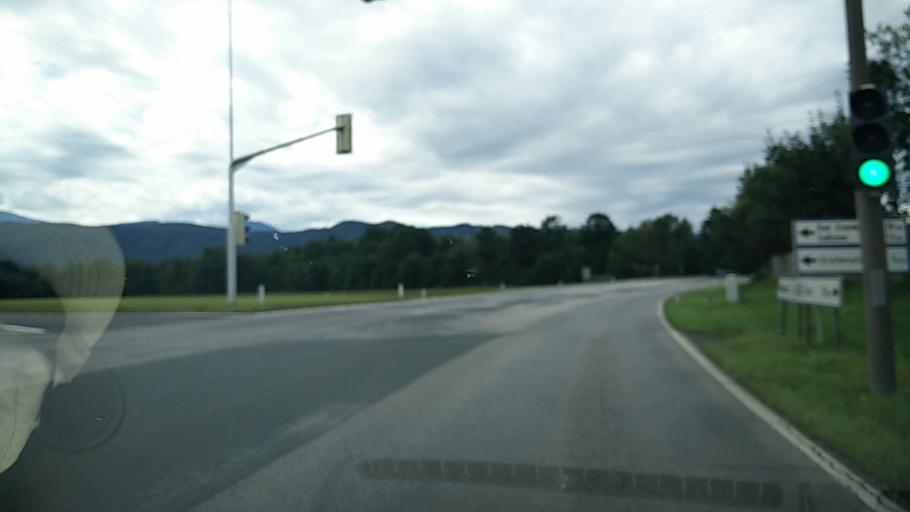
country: AT
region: Carinthia
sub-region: Politischer Bezirk Klagenfurt Land
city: Poggersdorf
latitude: 46.6299
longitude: 14.4155
